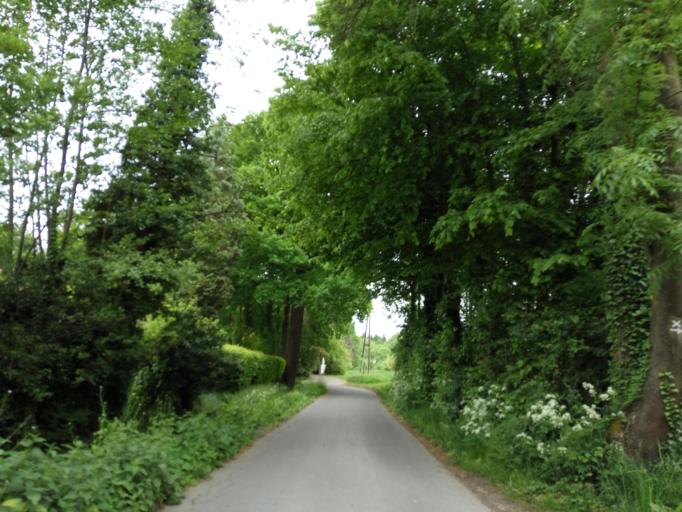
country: DE
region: North Rhine-Westphalia
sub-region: Regierungsbezirk Munster
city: Muenster
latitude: 51.9832
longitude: 7.5834
